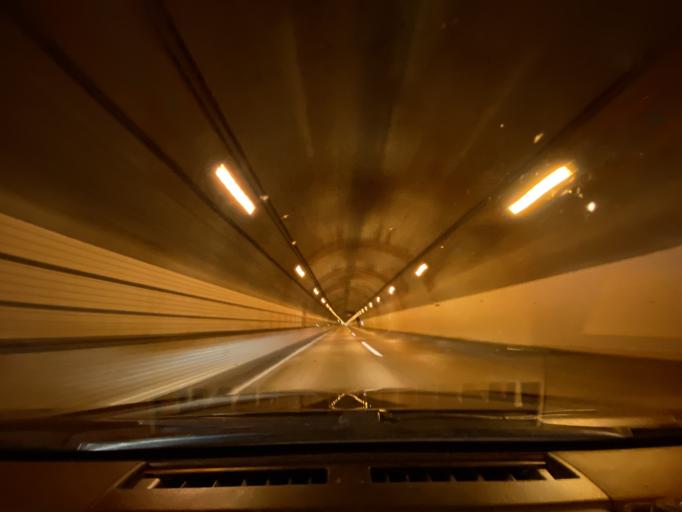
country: JP
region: Hokkaido
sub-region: Asahikawa-shi
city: Asahikawa
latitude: 43.7824
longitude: 142.2283
